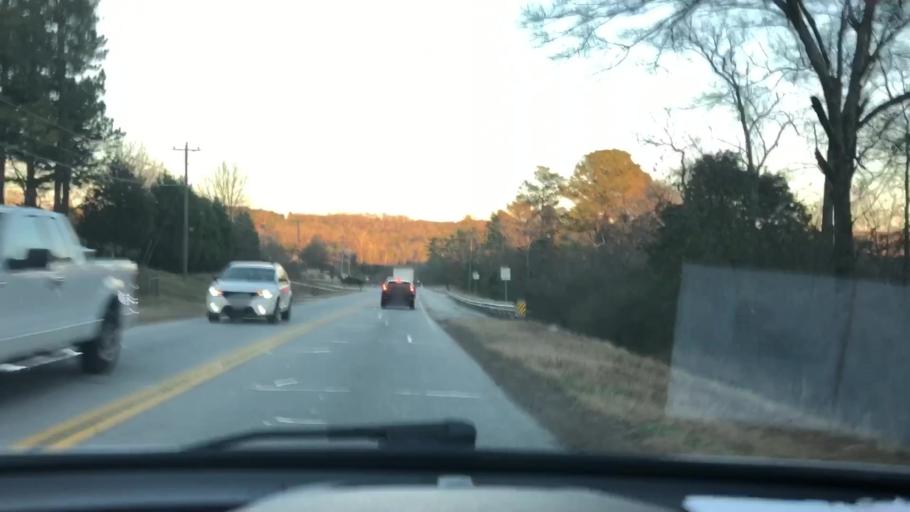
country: US
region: Georgia
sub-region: Walton County
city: Loganville
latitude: 33.8802
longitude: -83.8305
